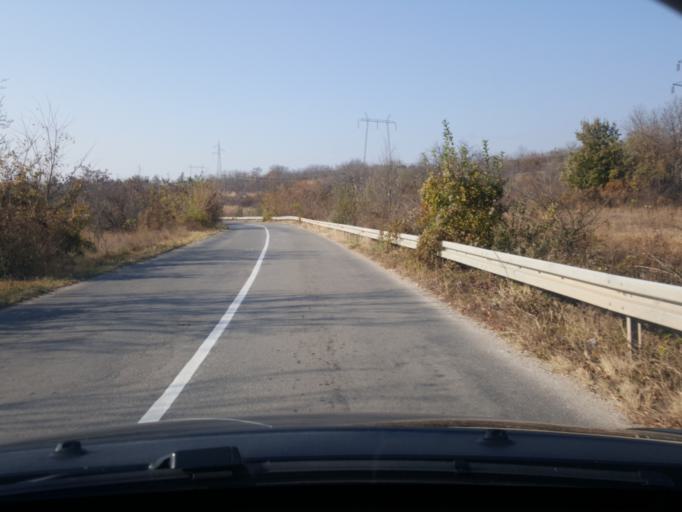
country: RS
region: Central Serbia
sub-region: Nisavski Okrug
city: Niska Banja
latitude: 43.3193
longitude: 22.0038
